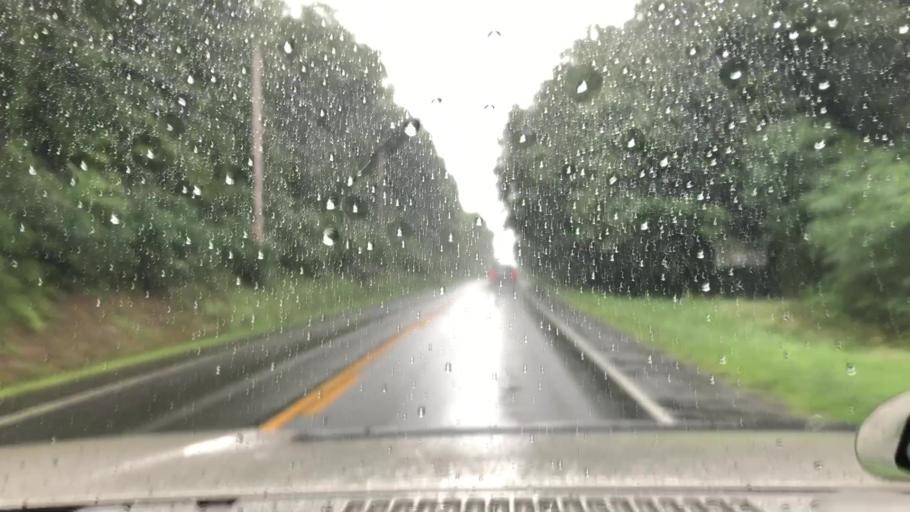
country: US
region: New York
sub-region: Greene County
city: Cairo
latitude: 42.2466
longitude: -73.9783
